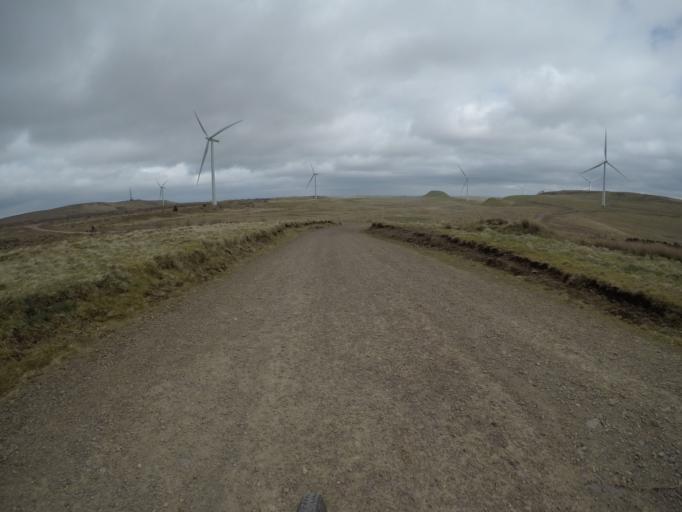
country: GB
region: Scotland
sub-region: East Renfrewshire
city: Eaglesham
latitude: 55.7062
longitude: -4.3308
